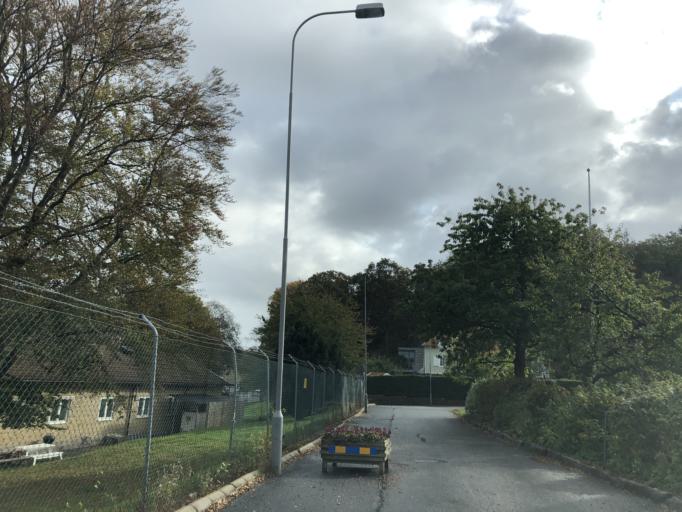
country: SE
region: Vaestra Goetaland
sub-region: Goteborg
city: Majorna
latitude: 57.6724
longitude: 11.8676
